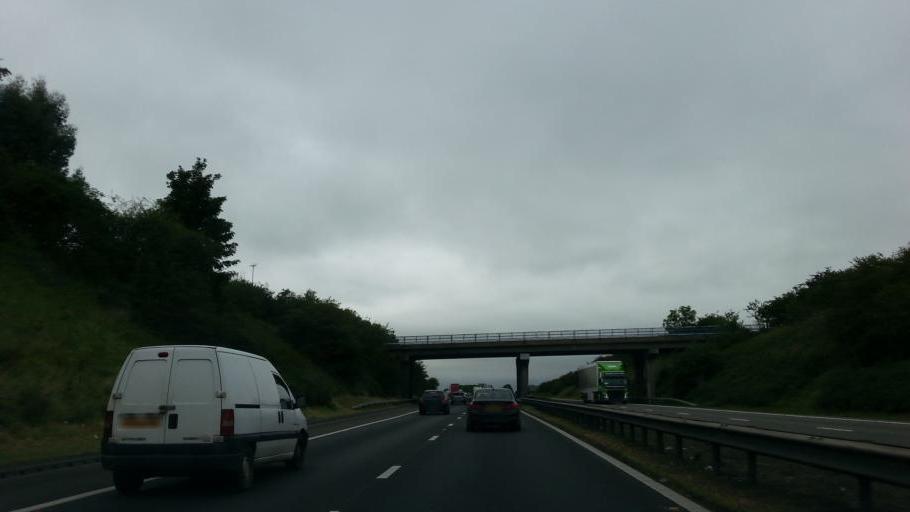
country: GB
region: England
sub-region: Nottinghamshire
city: Bircotes
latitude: 53.4083
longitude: -1.0817
